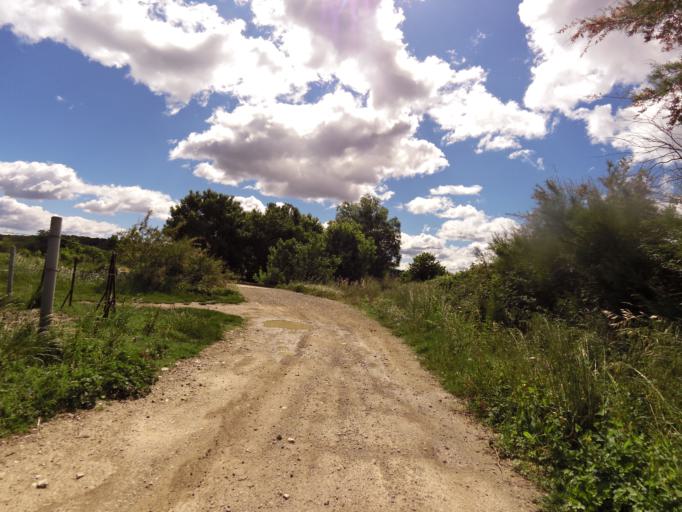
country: FR
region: Languedoc-Roussillon
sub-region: Departement du Gard
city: Vergeze
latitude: 43.7664
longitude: 4.2120
